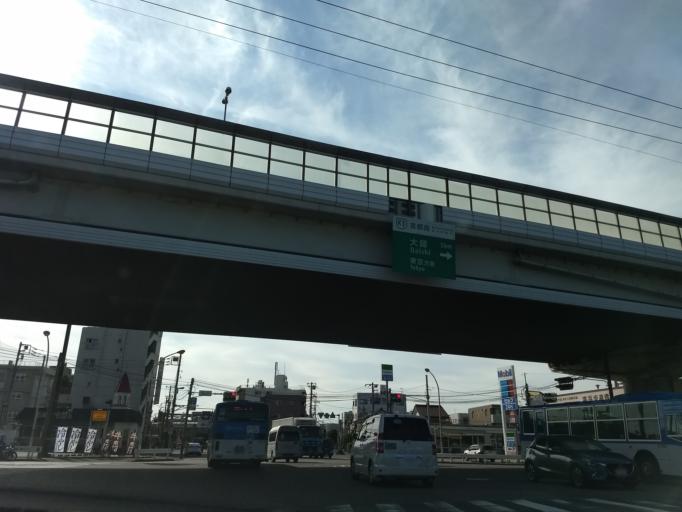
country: JP
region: Kanagawa
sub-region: Kawasaki-shi
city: Kawasaki
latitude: 35.5284
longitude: 139.7382
